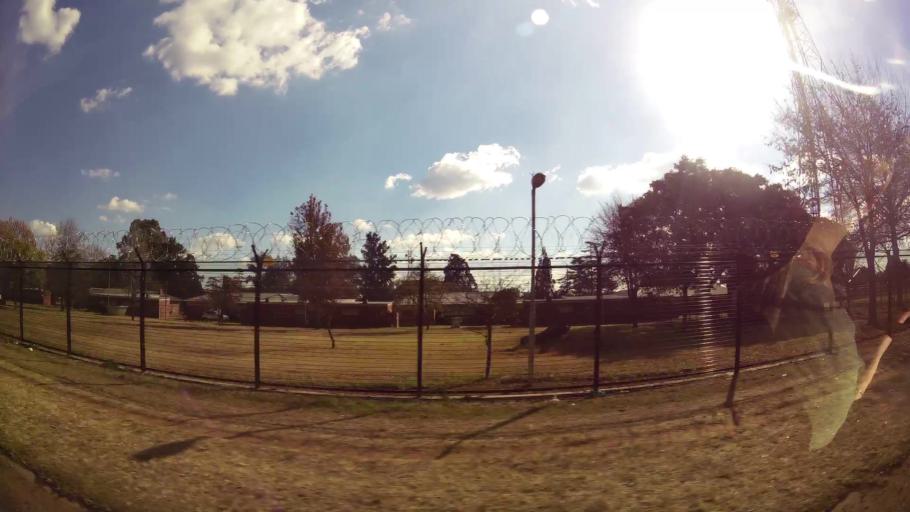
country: ZA
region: Mpumalanga
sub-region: Nkangala District Municipality
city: Witbank
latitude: -25.8878
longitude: 29.2215
